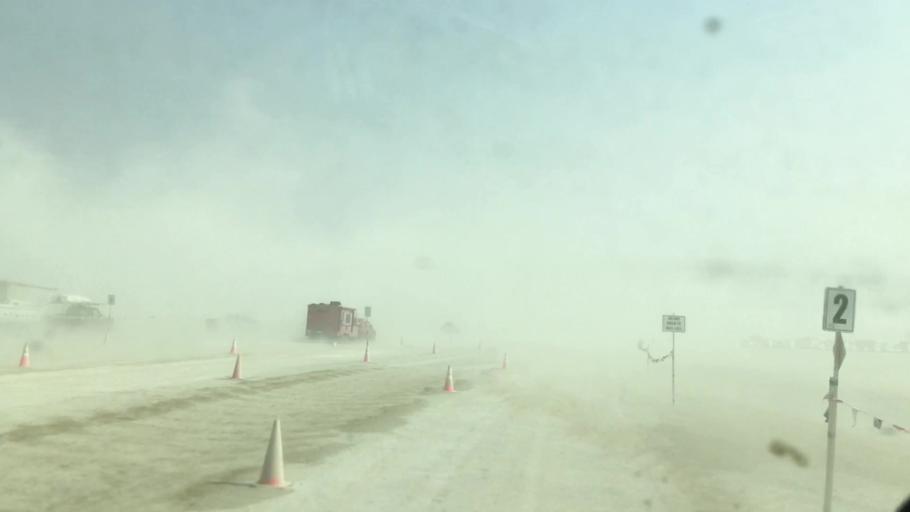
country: US
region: Nevada
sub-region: Pershing County
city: Lovelock
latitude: 40.7656
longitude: -119.2482
